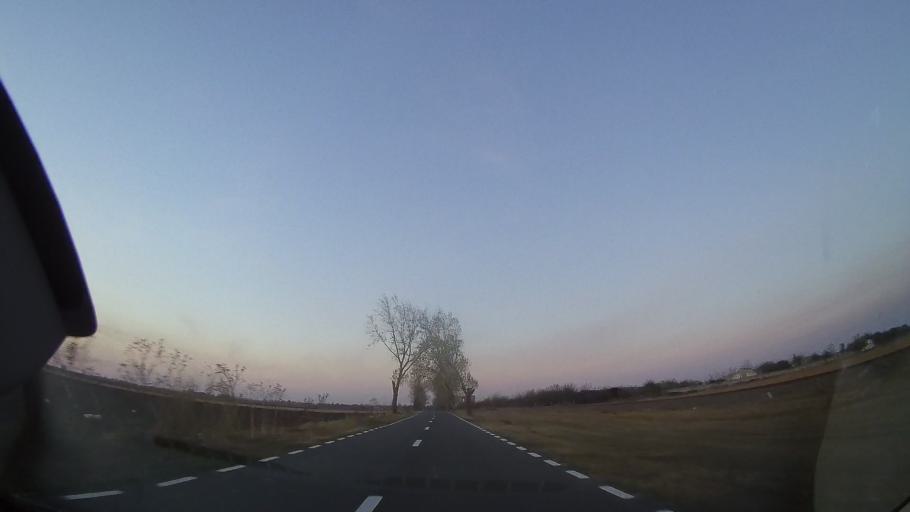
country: RO
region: Constanta
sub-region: Comuna Cobadin
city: Cobadin
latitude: 44.0432
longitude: 28.2547
